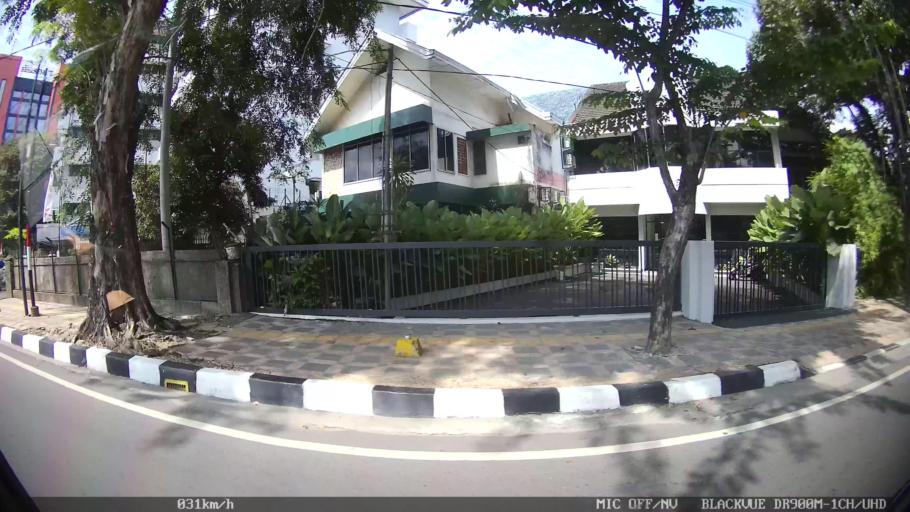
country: ID
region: North Sumatra
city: Medan
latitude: 3.5848
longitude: 98.6743
